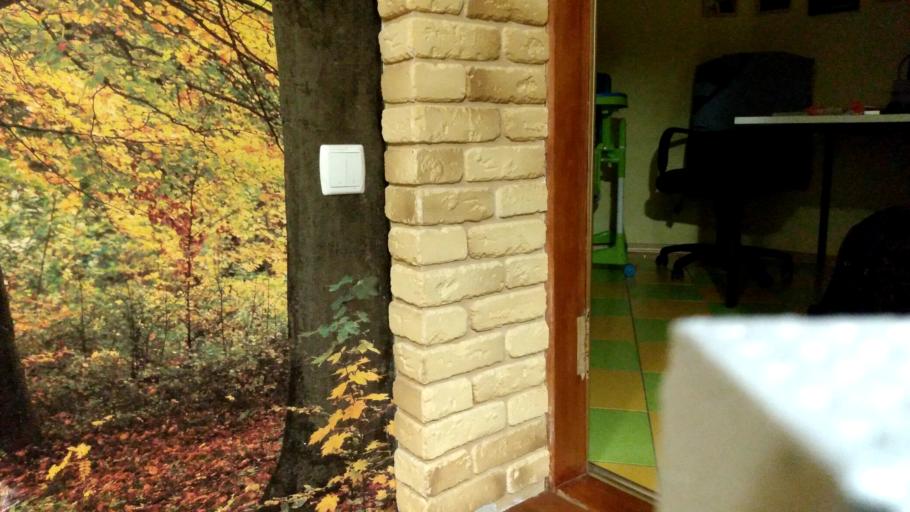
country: RU
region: Arkhangelskaya
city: Kargopol'
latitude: 61.5747
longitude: 37.7532
